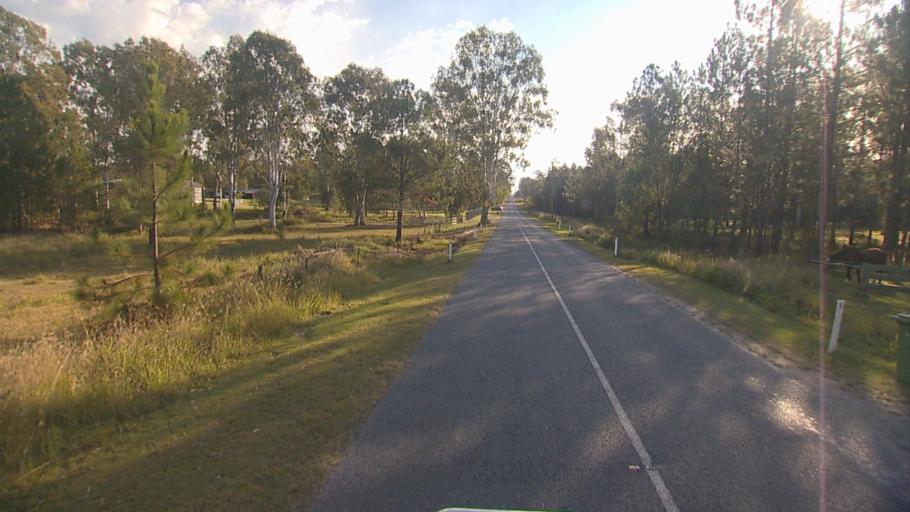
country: AU
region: Queensland
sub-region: Logan
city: Cedar Vale
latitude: -27.8495
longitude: 153.1164
